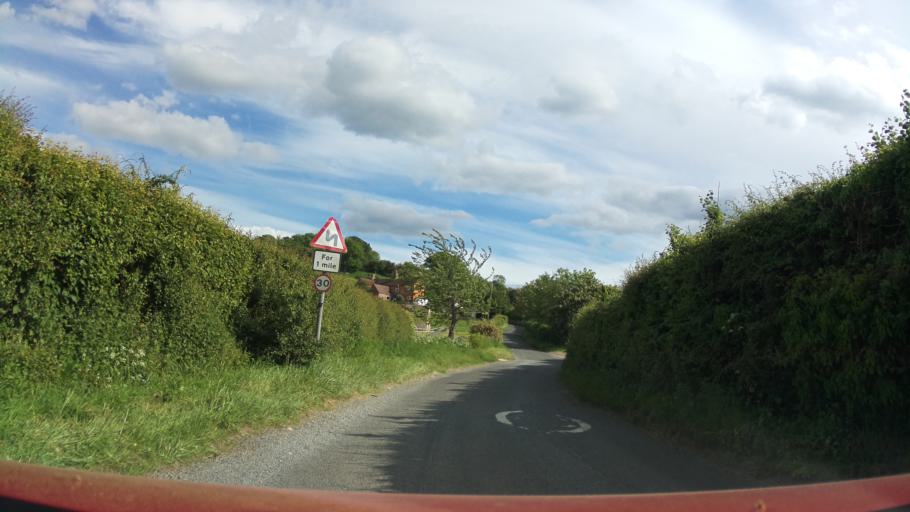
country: GB
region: England
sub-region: Gloucestershire
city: Chipping Campden
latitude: 52.0634
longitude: -1.8135
